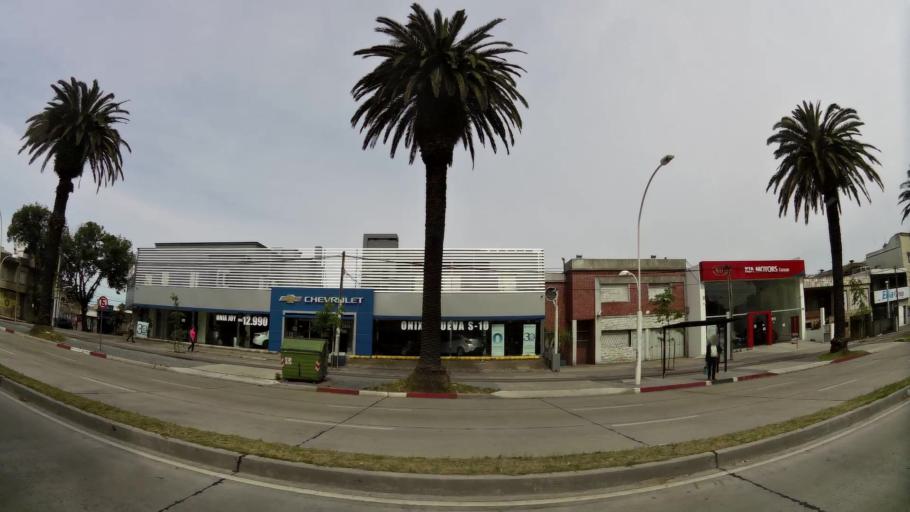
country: UY
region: Montevideo
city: Montevideo
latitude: -34.8724
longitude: -56.1673
